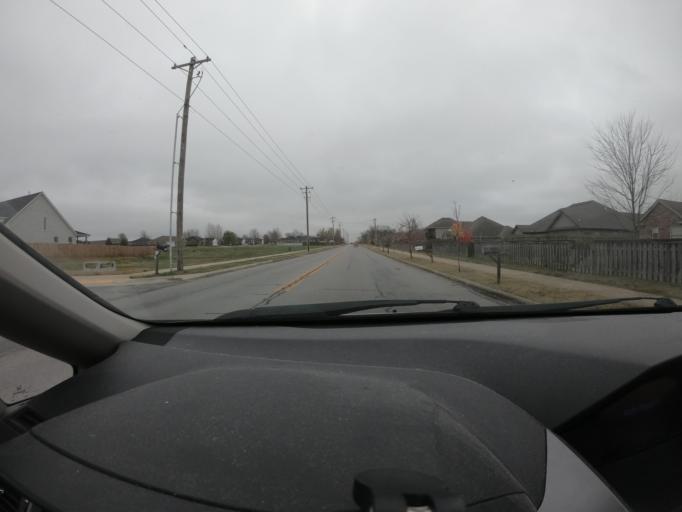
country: US
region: Arkansas
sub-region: Benton County
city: Bentonville
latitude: 36.3540
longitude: -94.2402
